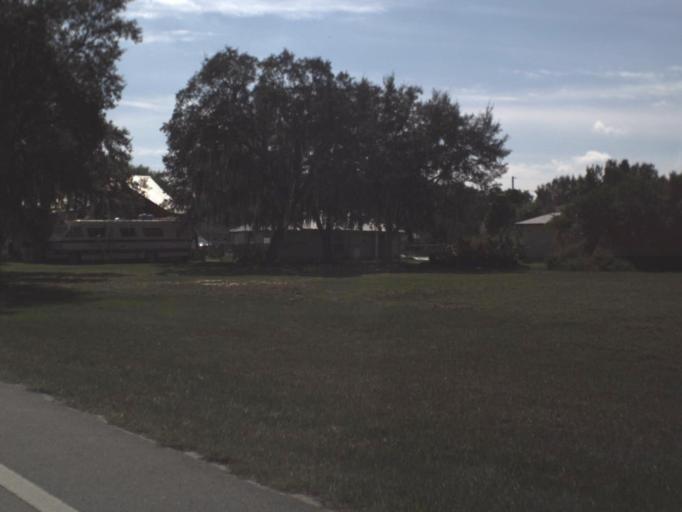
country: US
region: Florida
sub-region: Highlands County
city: Sebring
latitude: 27.5135
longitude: -81.4520
